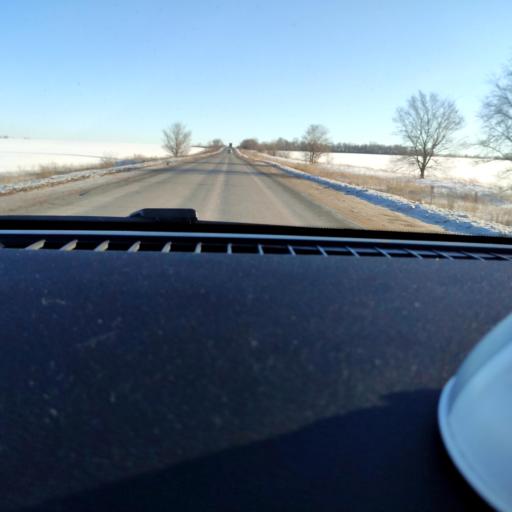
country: RU
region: Samara
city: Spiridonovka
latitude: 53.1444
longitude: 50.5536
